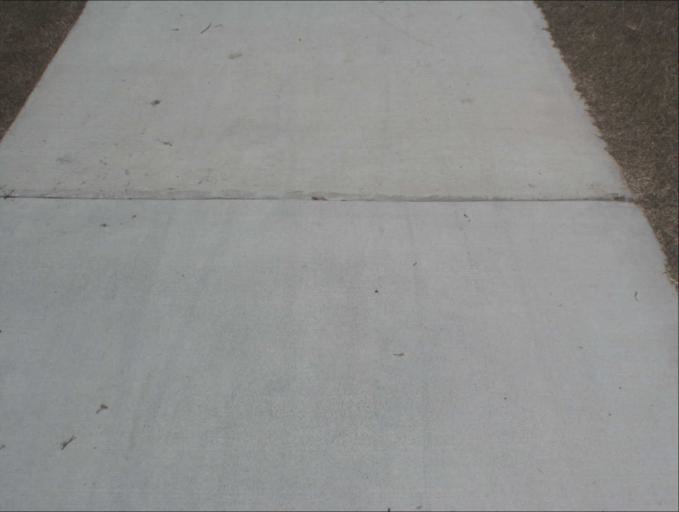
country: AU
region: Queensland
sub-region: Logan
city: North Maclean
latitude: -27.8145
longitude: 152.9649
